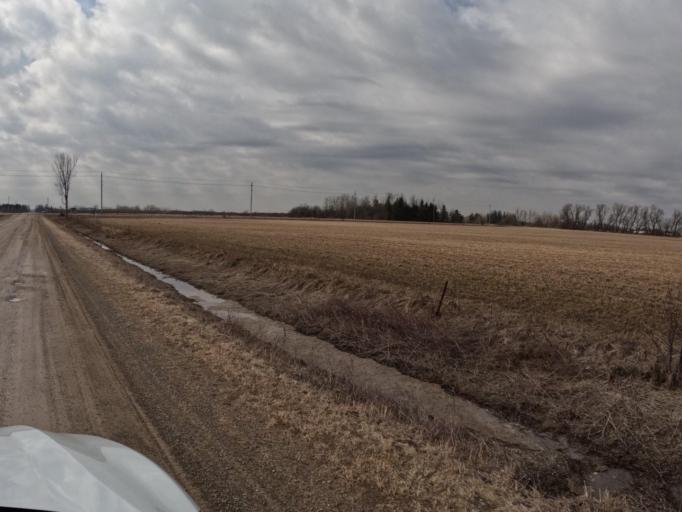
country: CA
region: Ontario
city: Orangeville
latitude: 43.9225
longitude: -80.2184
